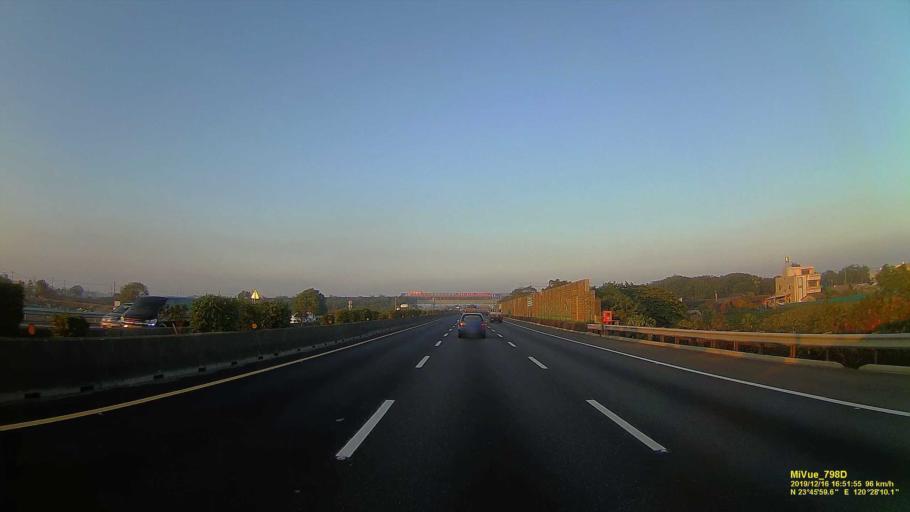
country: TW
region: Taiwan
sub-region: Yunlin
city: Douliu
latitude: 23.7672
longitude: 120.4697
